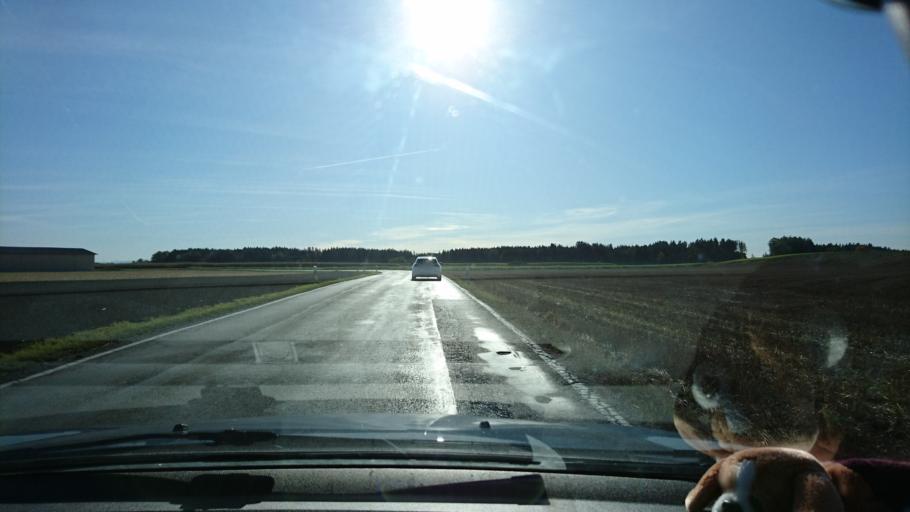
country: DE
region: Bavaria
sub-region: Upper Bavaria
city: Anzing
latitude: 48.1265
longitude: 11.8328
